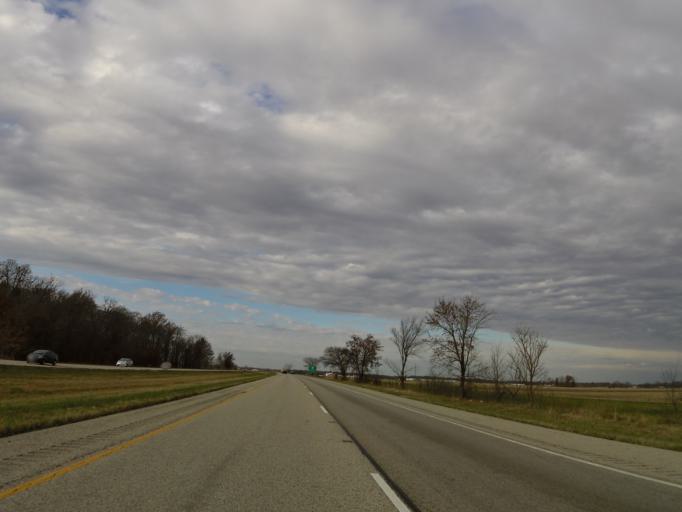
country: US
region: Illinois
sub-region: Washington County
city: Nashville
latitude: 38.3912
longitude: -89.3436
